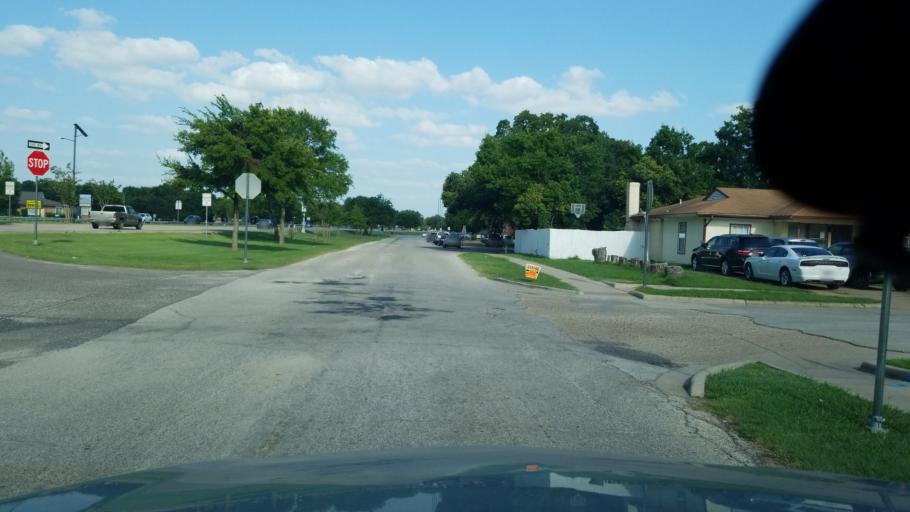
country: US
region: Texas
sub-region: Dallas County
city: Irving
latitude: 32.8268
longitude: -96.9727
